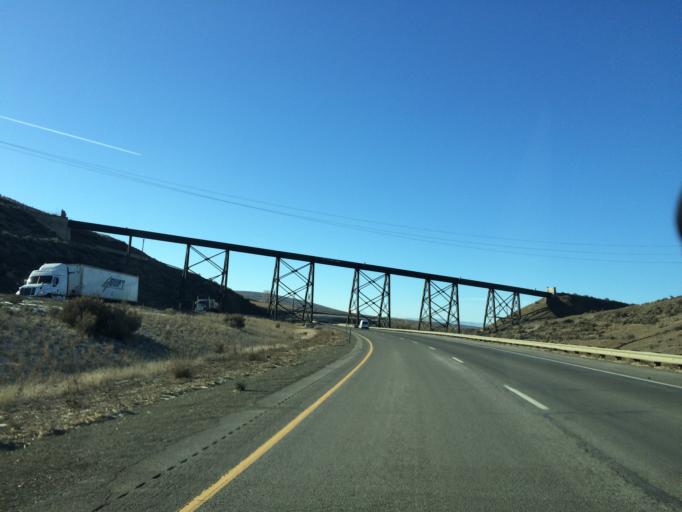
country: US
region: Washington
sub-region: Kittitas County
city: Kittitas
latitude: 46.9567
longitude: -120.3010
